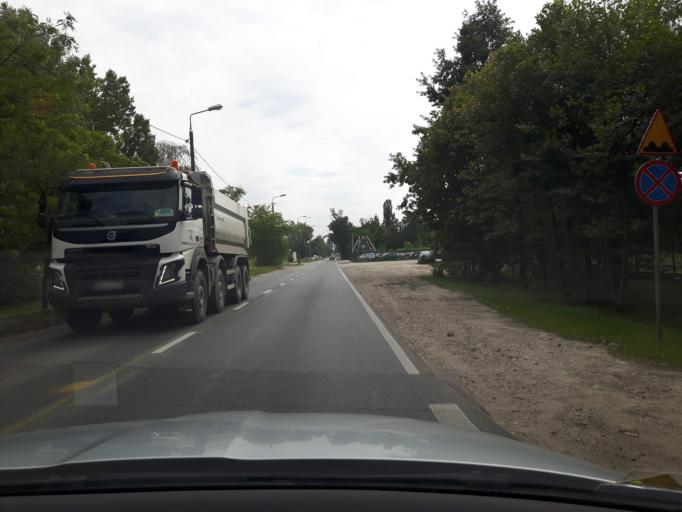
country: PL
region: Masovian Voivodeship
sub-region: Powiat wolominski
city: Zabki
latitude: 52.2731
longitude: 21.1179
